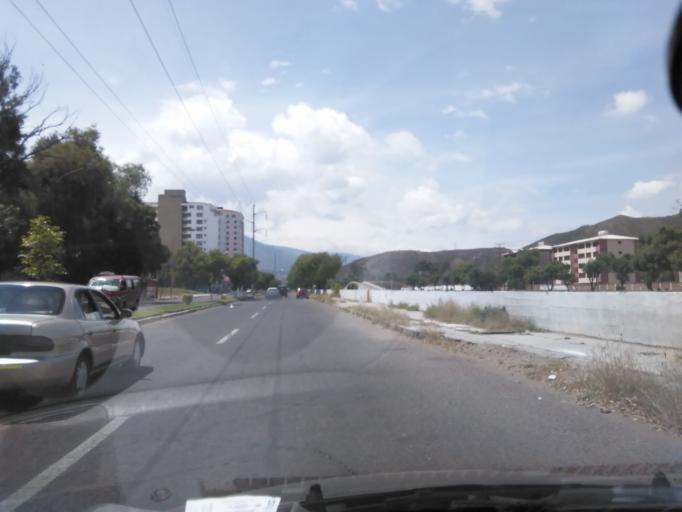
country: BO
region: Cochabamba
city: Cochabamba
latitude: -17.3779
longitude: -66.1465
